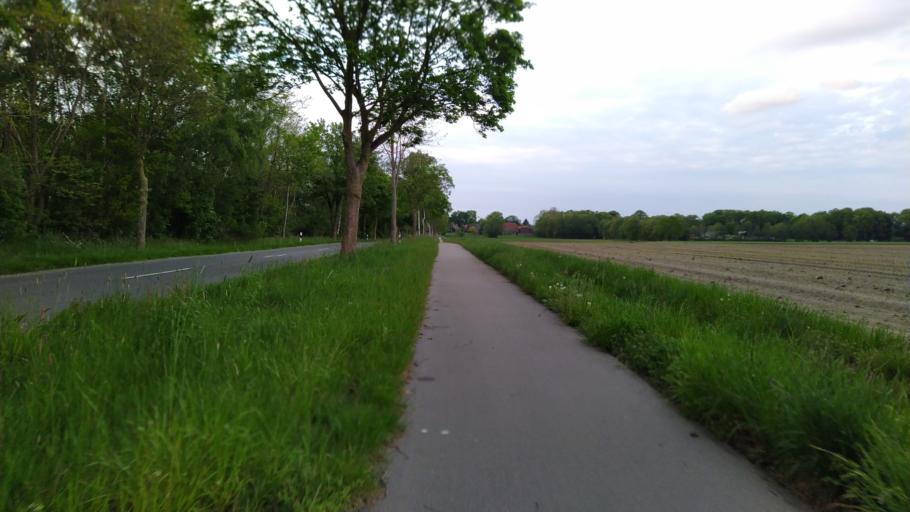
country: DE
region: Lower Saxony
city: Ahlerstedt
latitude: 53.3977
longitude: 9.4045
